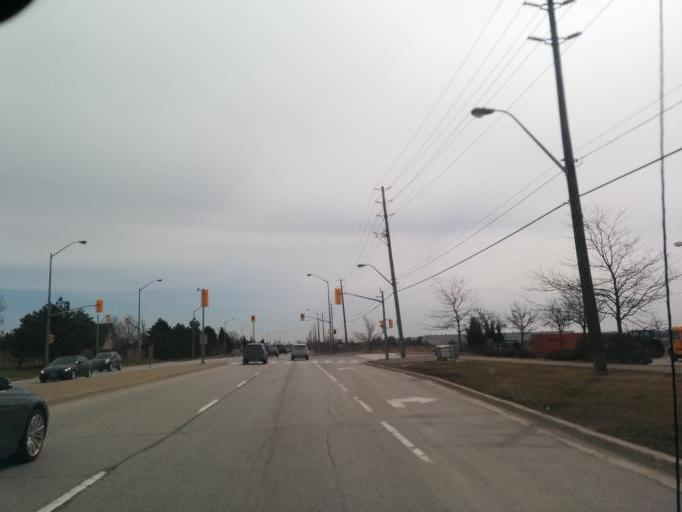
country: CA
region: Ontario
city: Brampton
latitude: 43.7245
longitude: -79.8124
